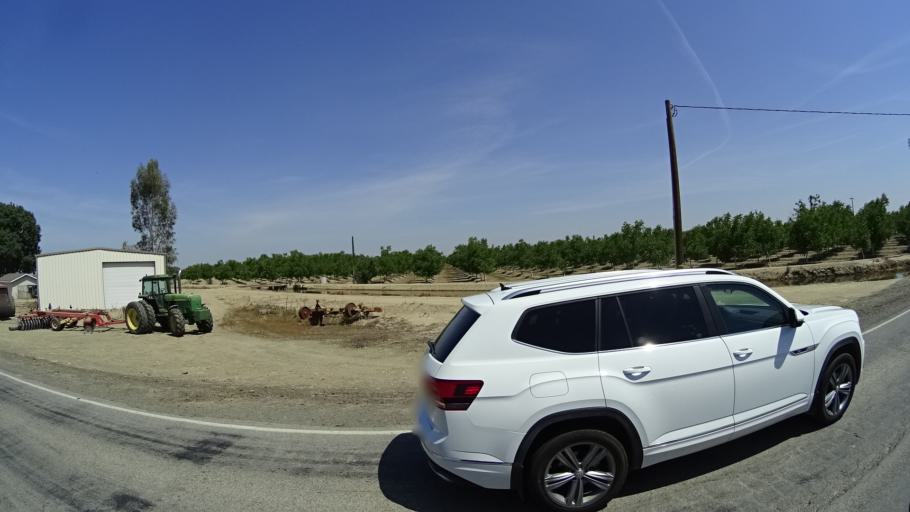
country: US
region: California
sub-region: Fresno County
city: Riverdale
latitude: 36.4020
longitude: -119.8243
